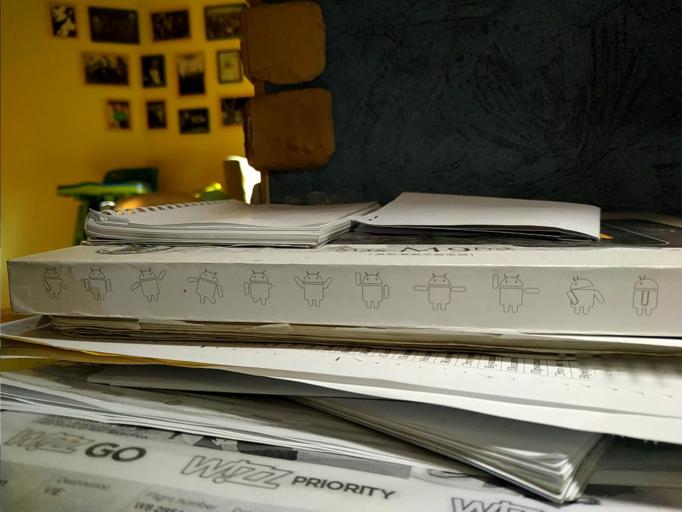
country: RU
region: Novgorod
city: Poddor'ye
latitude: 57.4329
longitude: 31.0393
